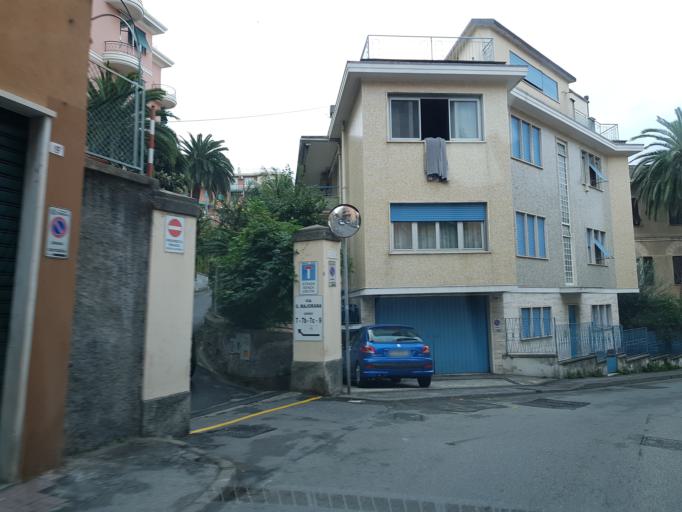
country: IT
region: Liguria
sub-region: Provincia di Genova
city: Bogliasco
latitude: 44.3869
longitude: 9.0114
